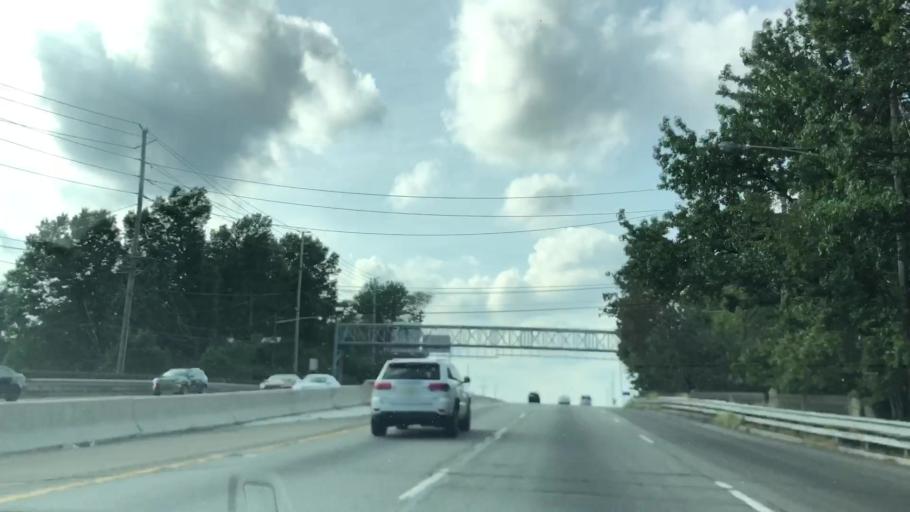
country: US
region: New Jersey
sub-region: Essex County
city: Nutley
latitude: 40.8343
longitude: -74.1480
